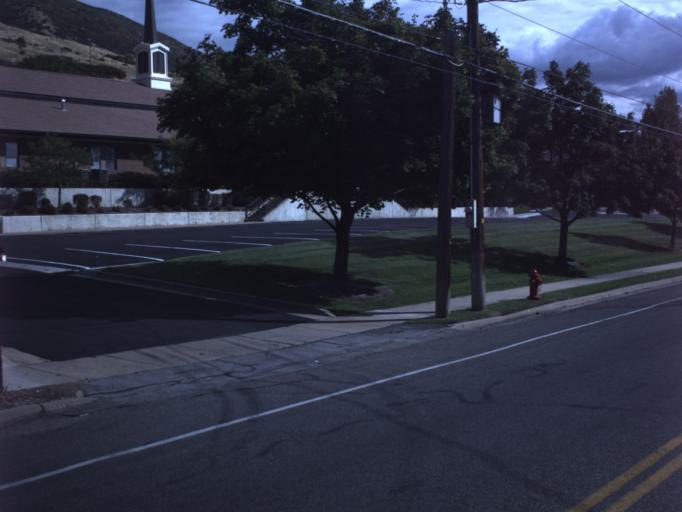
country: US
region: Utah
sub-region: Davis County
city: Farmington
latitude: 40.9580
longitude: -111.8834
